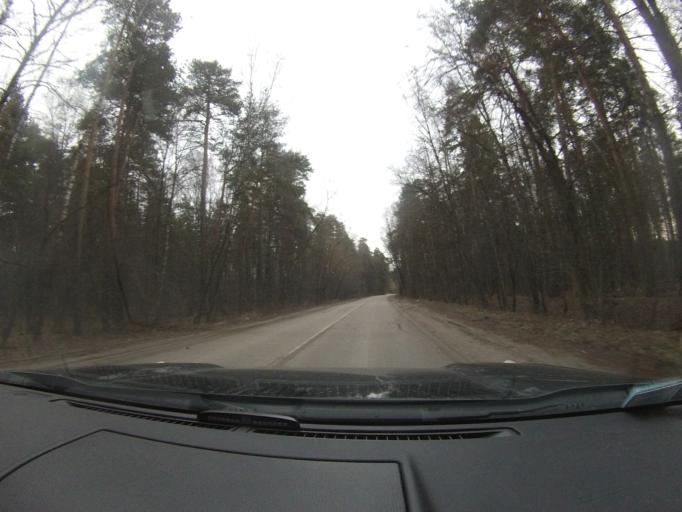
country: RU
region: Moskovskaya
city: Voskresensk
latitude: 55.3366
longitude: 38.6745
